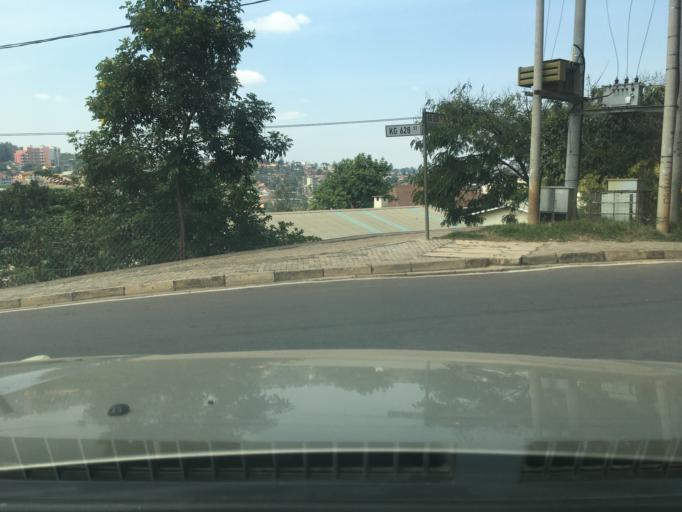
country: RW
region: Kigali
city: Kigali
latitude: -1.9543
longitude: 30.0984
